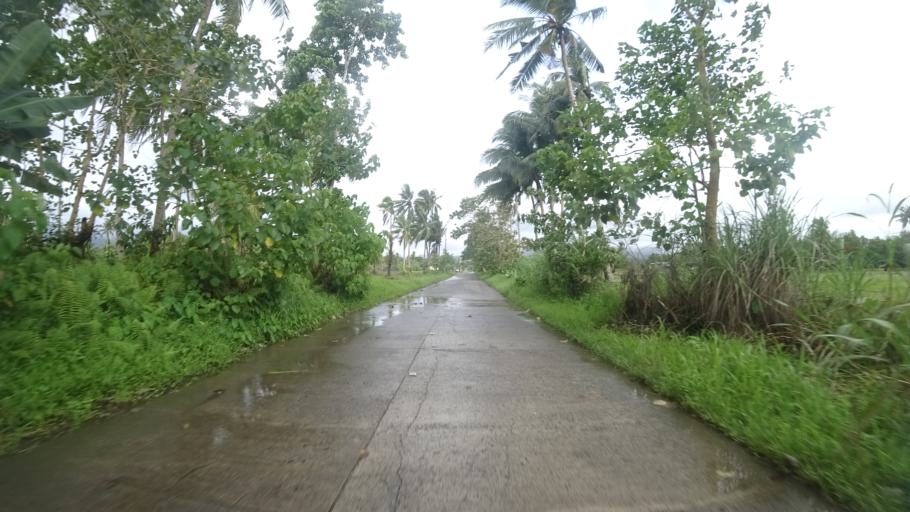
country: PH
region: Eastern Visayas
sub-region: Province of Leyte
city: Bugho
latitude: 10.8210
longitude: 124.9409
